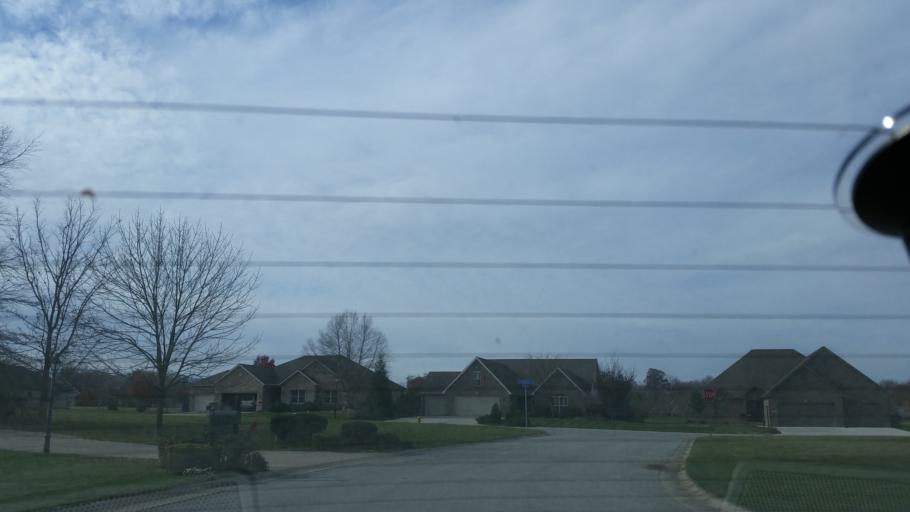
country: US
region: Indiana
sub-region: Howard County
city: Indian Heights
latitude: 40.4282
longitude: -86.1555
